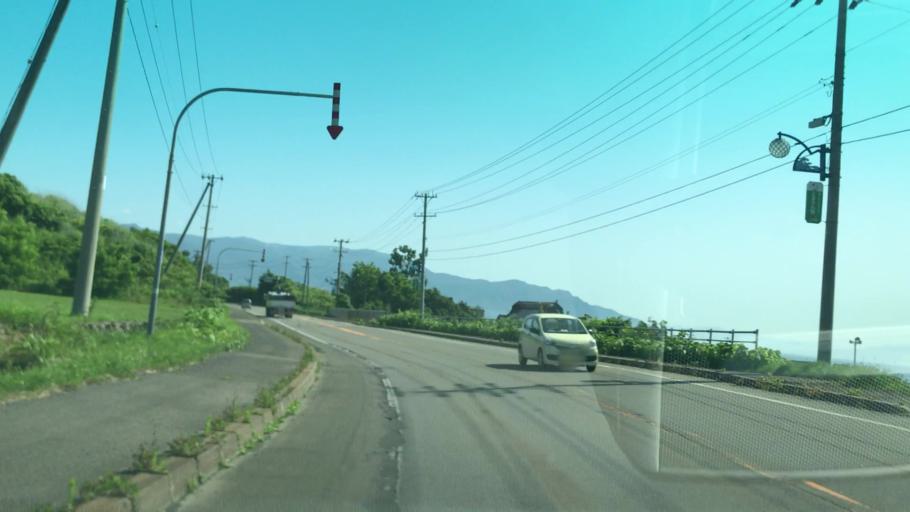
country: JP
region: Hokkaido
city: Iwanai
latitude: 43.0620
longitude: 140.4974
